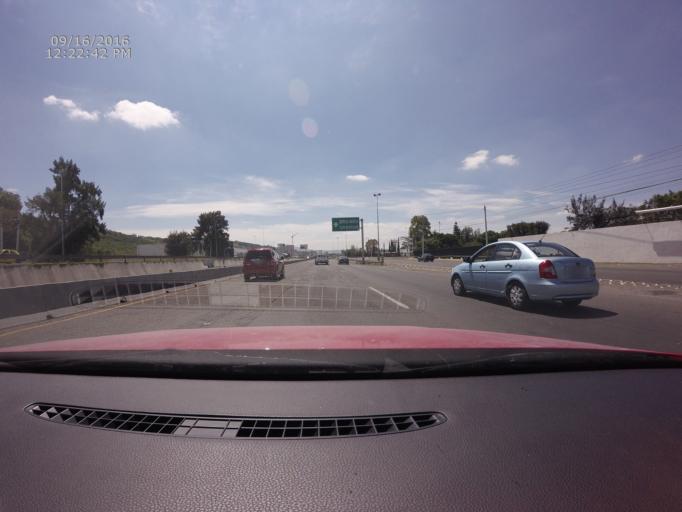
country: MX
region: Queretaro
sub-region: Queretaro
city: Sergio Villasenor
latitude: 20.6355
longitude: -100.4283
